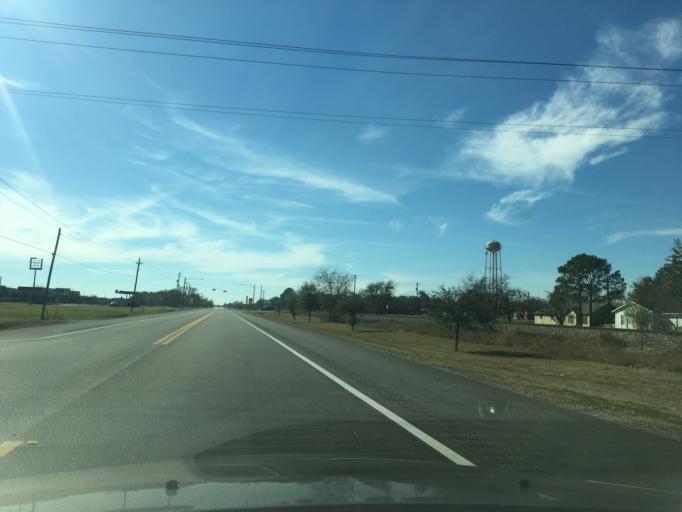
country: US
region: Texas
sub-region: Wharton County
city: East Bernard
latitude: 29.4484
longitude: -95.9987
